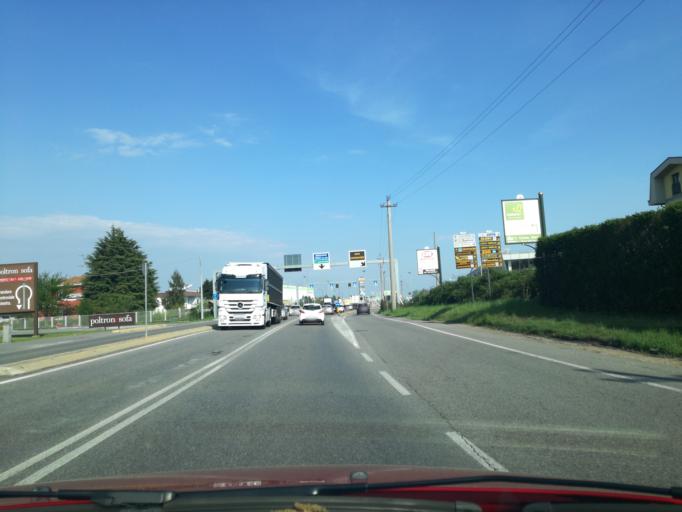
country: IT
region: Lombardy
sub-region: Provincia di Monza e Brianza
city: Busnago
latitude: 45.6201
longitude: 9.4676
